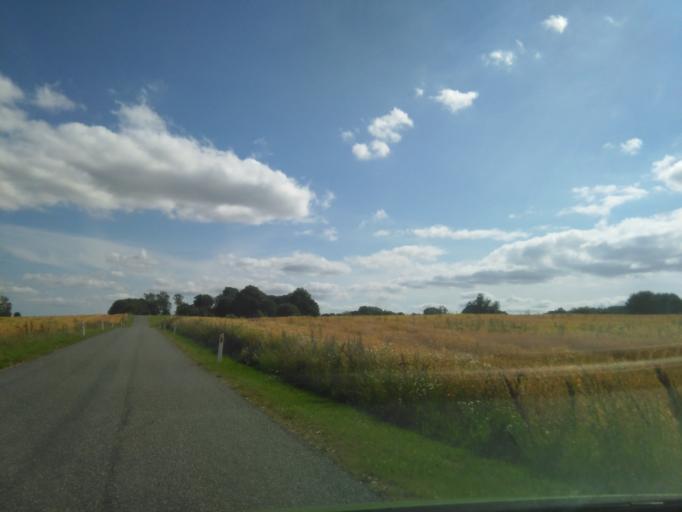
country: DK
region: Central Jutland
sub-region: Arhus Kommune
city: Framlev
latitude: 56.1195
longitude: 10.0180
